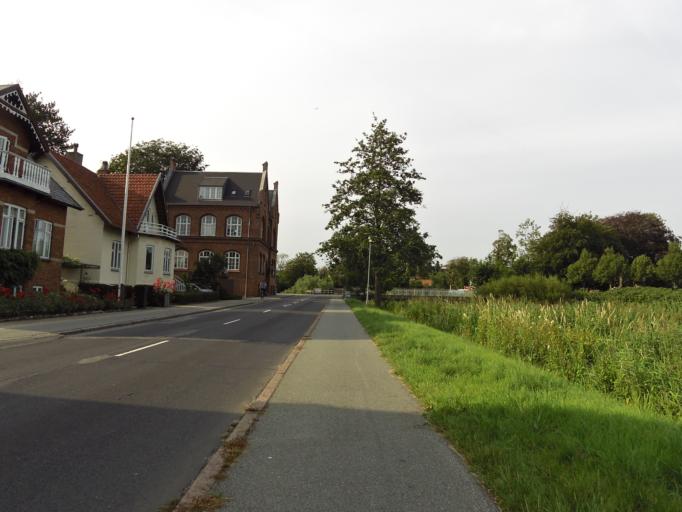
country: DK
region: South Denmark
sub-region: Esbjerg Kommune
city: Ribe
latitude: 55.3270
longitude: 8.7671
